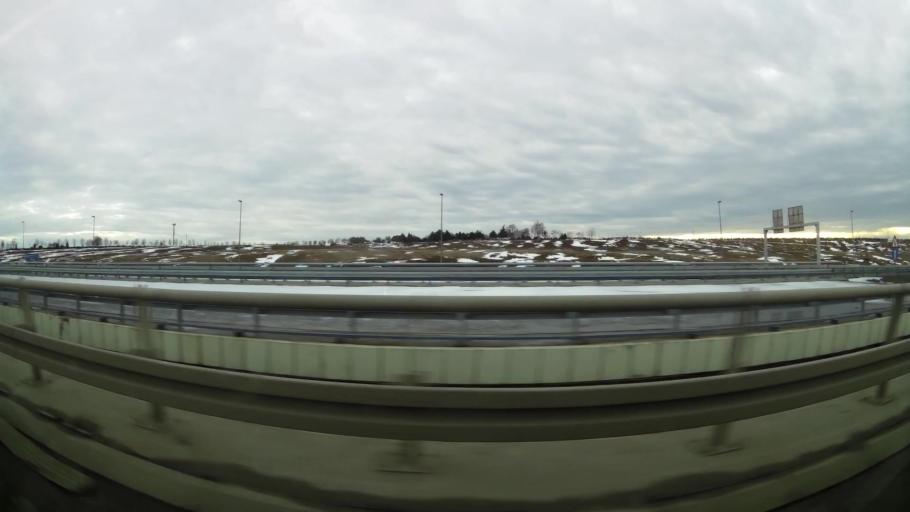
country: RS
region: Central Serbia
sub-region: Belgrade
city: Rakovica
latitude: 44.7145
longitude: 20.4101
